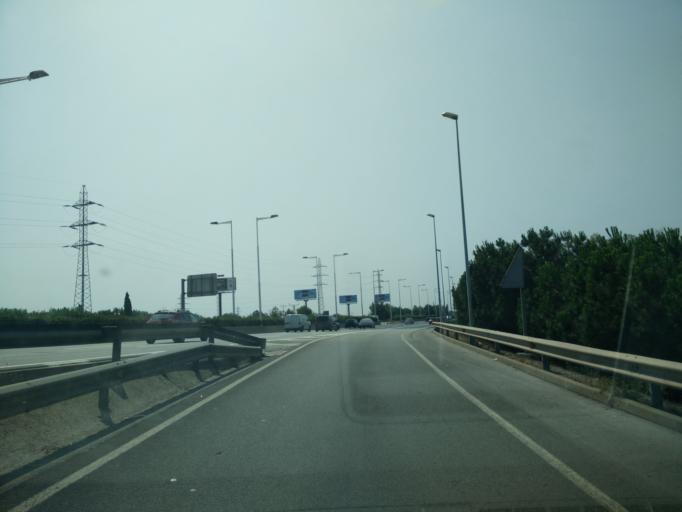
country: ES
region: Catalonia
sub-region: Provincia de Barcelona
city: Cornella de Llobregat
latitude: 41.3516
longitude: 2.0915
